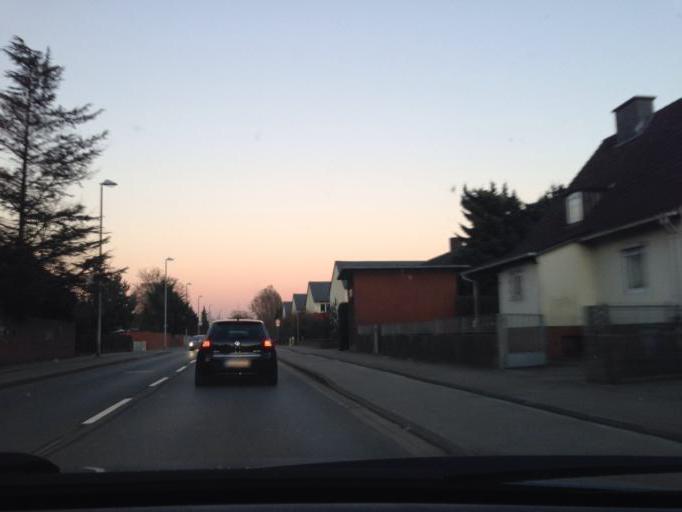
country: DE
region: Lower Saxony
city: Celle
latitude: 52.6091
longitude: 10.0822
